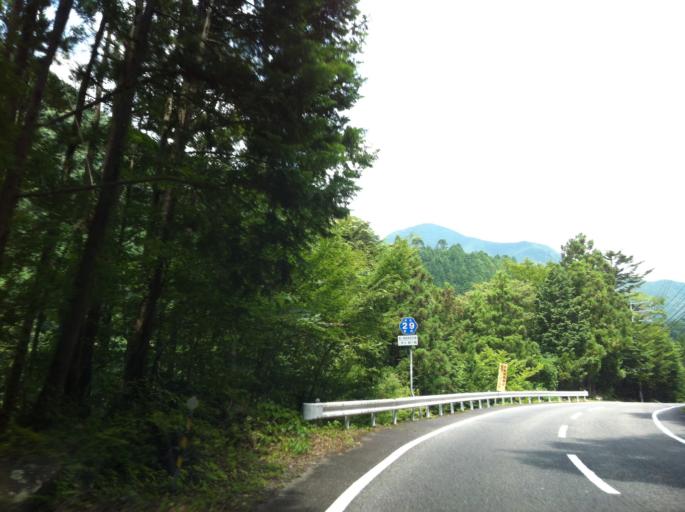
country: JP
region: Shizuoka
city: Fujinomiya
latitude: 35.2706
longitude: 138.3263
